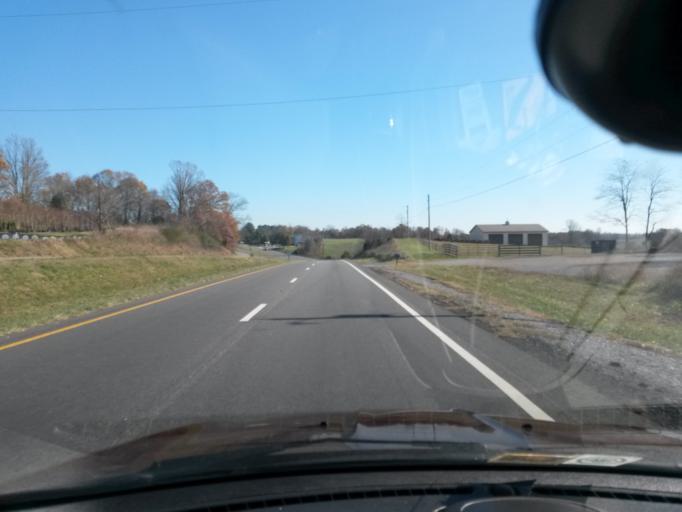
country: US
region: Virginia
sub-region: City of Bedford
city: Bedford
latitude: 37.3191
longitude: -79.4314
